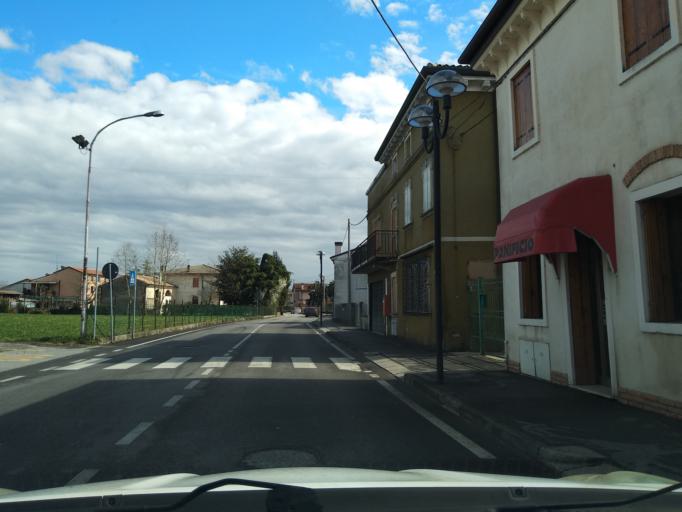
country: IT
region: Veneto
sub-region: Provincia di Vicenza
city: Bolzano Vicentino
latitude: 45.6011
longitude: 11.6144
